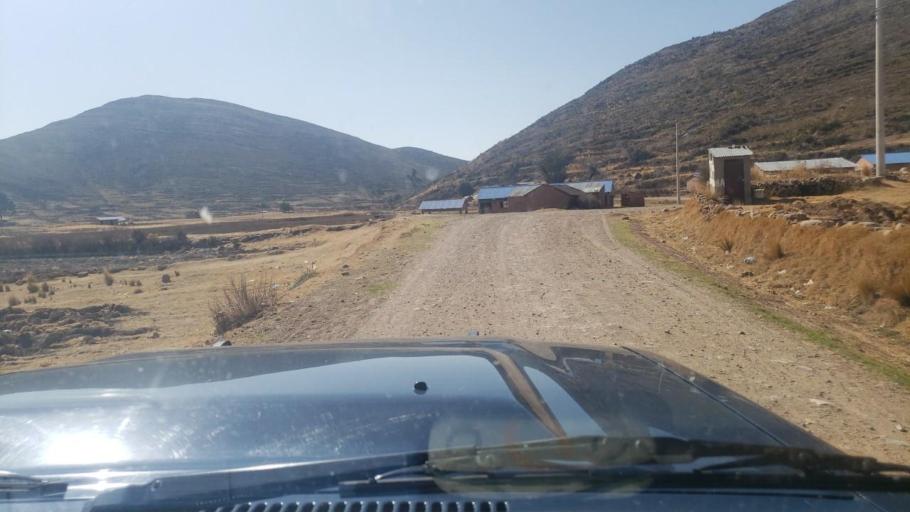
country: BO
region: La Paz
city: Huatajata
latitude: -16.3394
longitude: -68.6769
